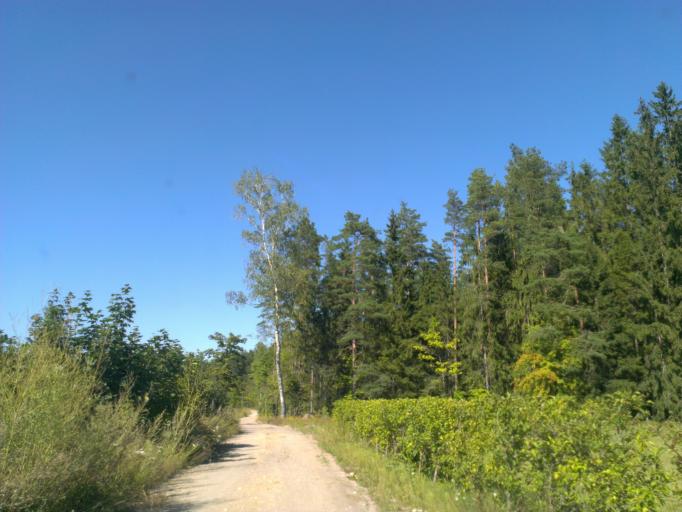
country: LV
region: Sigulda
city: Sigulda
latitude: 57.1034
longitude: 24.8161
